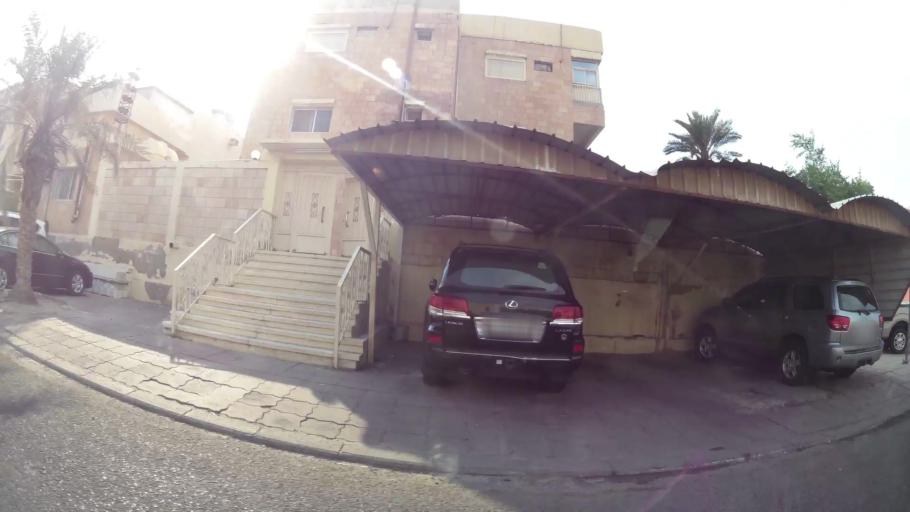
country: KW
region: Al Asimah
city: Ash Shamiyah
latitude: 29.3129
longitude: 47.9839
